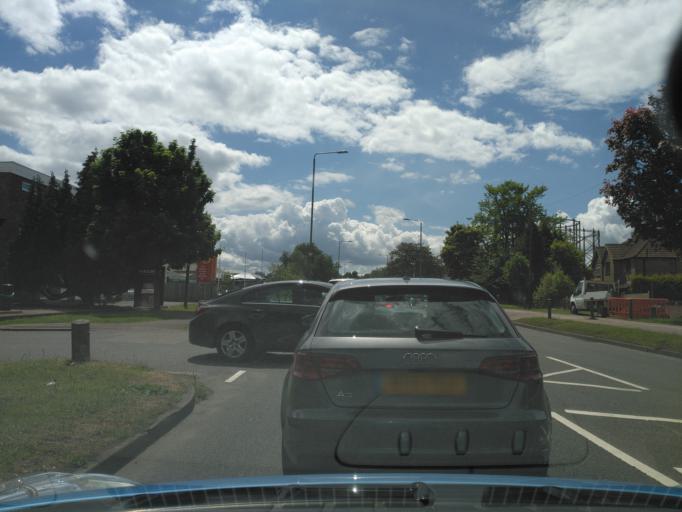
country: GB
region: England
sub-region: Greater London
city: Sidcup
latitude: 51.4009
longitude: 0.1132
